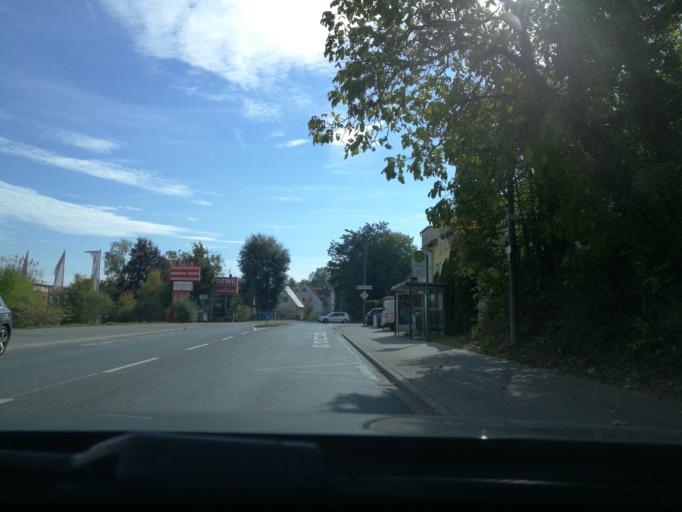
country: DE
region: Bavaria
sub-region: Regierungsbezirk Mittelfranken
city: Furth
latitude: 49.4951
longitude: 10.9744
